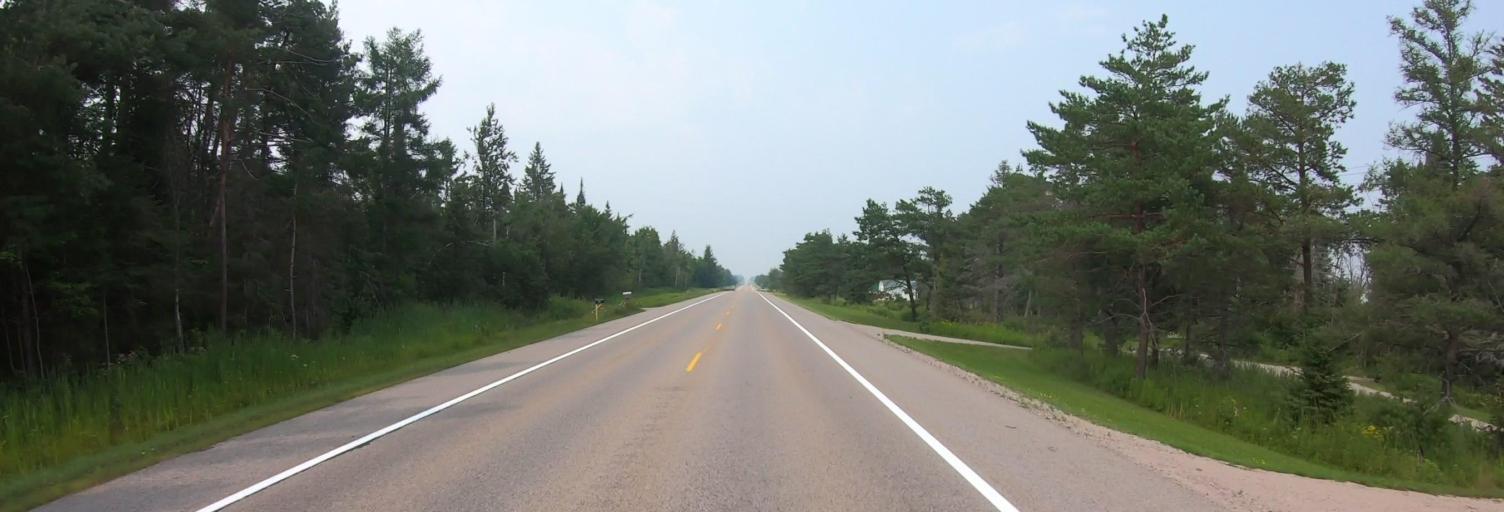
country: US
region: Michigan
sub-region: Chippewa County
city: Sault Ste. Marie
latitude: 46.2634
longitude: -84.3635
